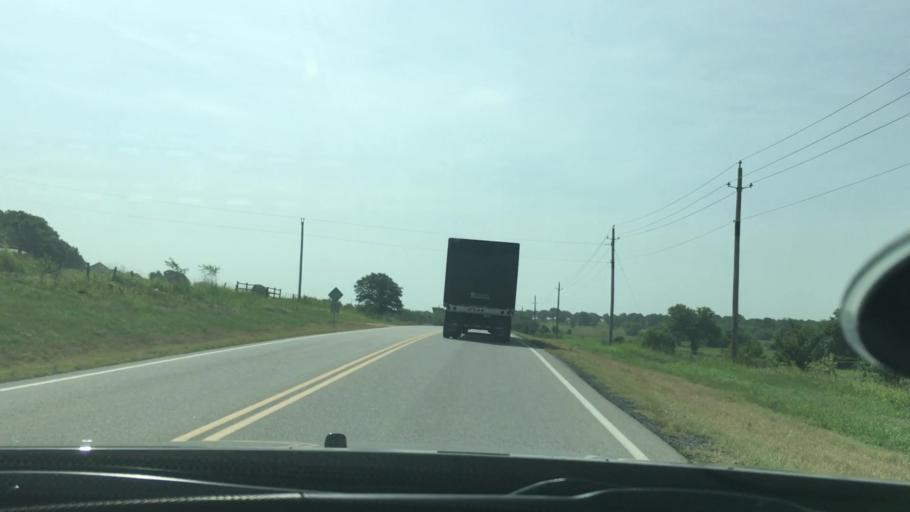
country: US
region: Oklahoma
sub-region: Atoka County
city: Atoka
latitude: 34.4016
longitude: -96.1748
